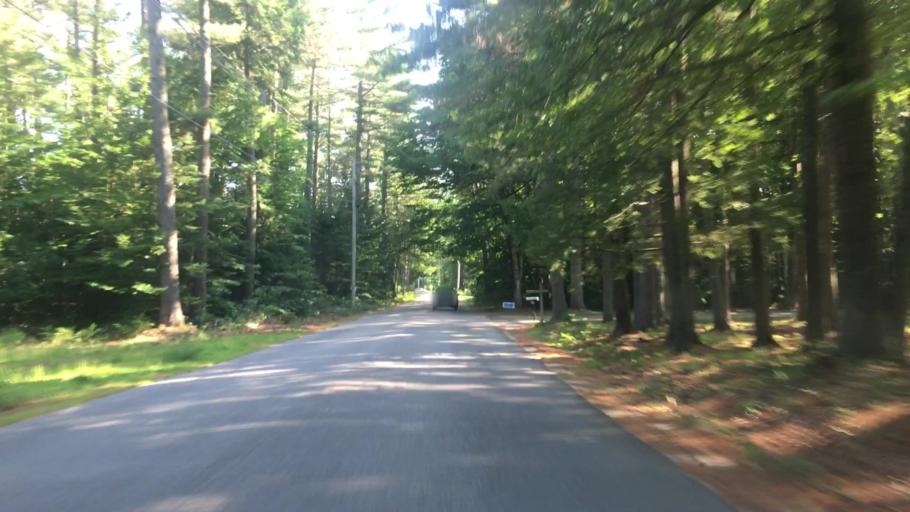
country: US
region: Maine
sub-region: York County
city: Buxton
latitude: 43.7169
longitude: -70.5160
